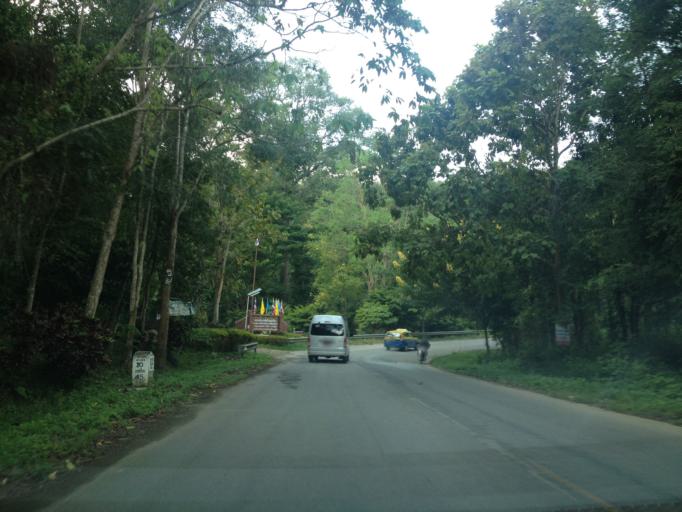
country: TH
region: Chiang Mai
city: Samoeng
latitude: 18.7943
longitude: 98.8329
